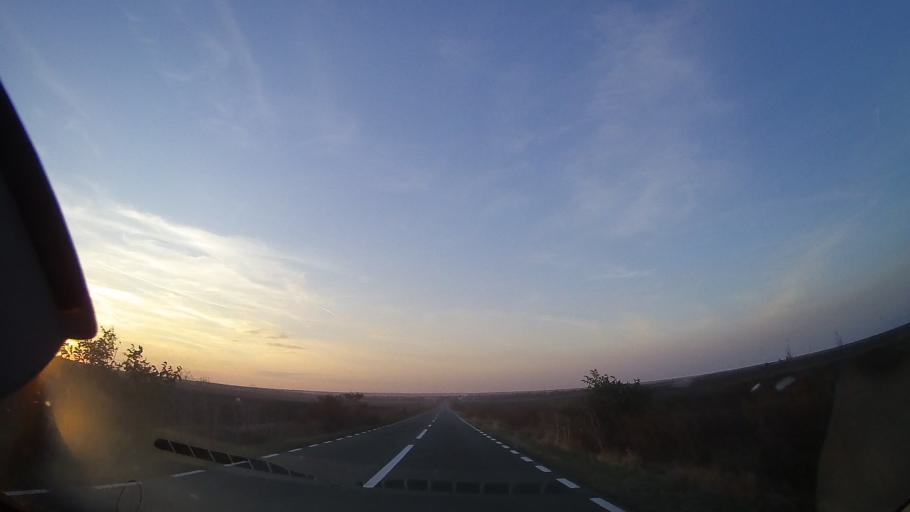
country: RO
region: Constanta
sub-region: Comuna Topraisar
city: Topraisar
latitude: 44.0235
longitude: 28.4078
